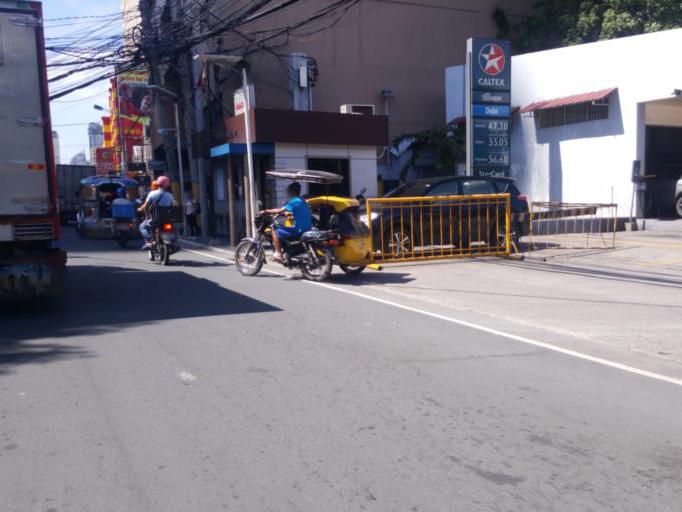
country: PH
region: Metro Manila
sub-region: City of Manila
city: Port Area
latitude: 14.5653
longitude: 120.9867
